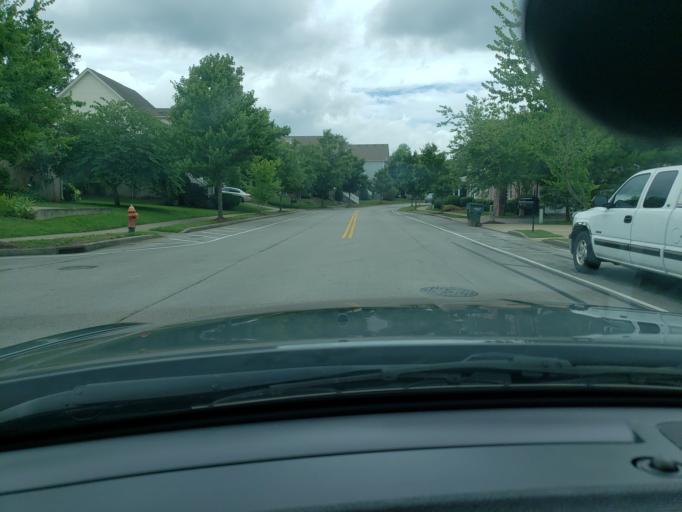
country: US
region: Tennessee
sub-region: Williamson County
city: Nolensville
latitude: 36.0178
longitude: -86.7024
